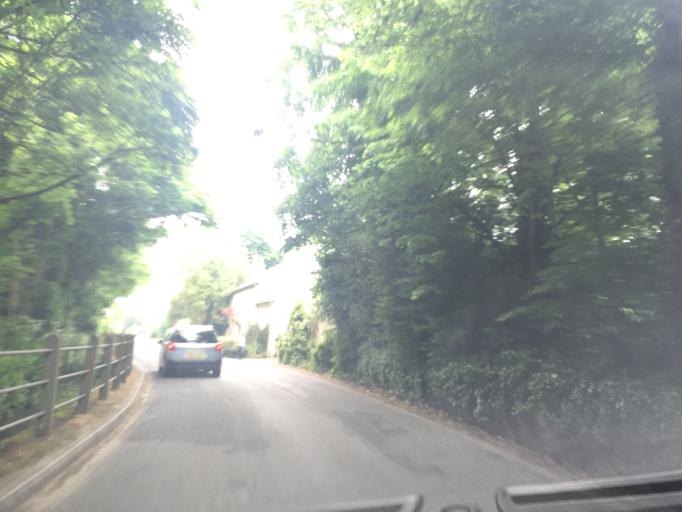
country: GB
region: England
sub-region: Dorset
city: Bovington Camp
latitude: 50.6646
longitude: -2.2763
